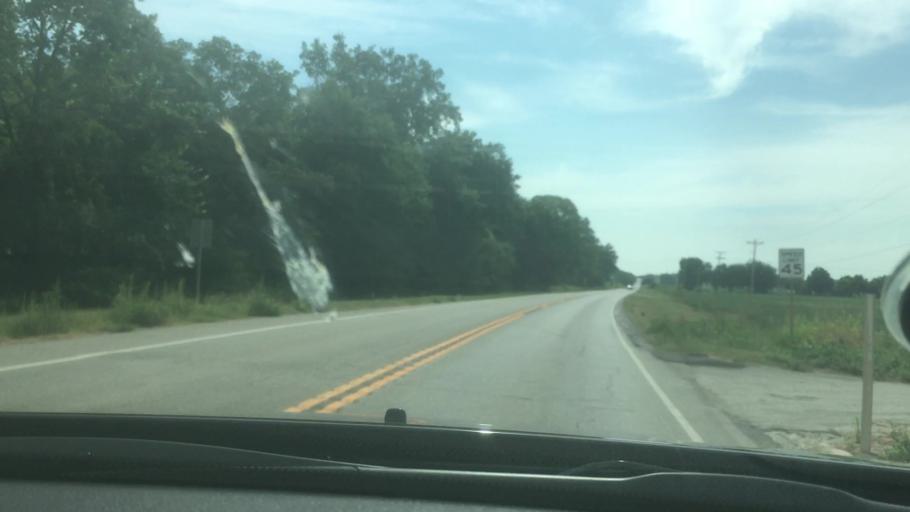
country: US
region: Oklahoma
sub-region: Garvin County
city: Maysville
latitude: 34.8170
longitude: -97.4011
